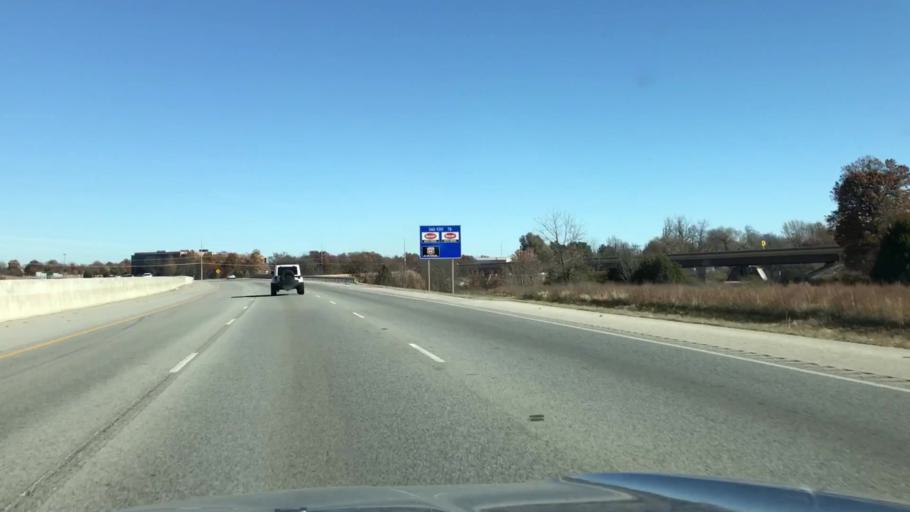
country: US
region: Arkansas
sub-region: Benton County
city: Lowell
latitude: 36.2394
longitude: -94.1565
